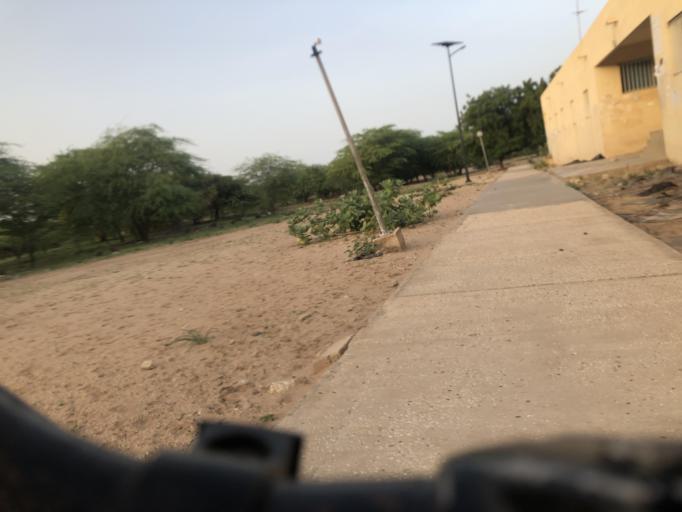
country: SN
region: Saint-Louis
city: Saint-Louis
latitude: 16.0678
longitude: -16.4222
